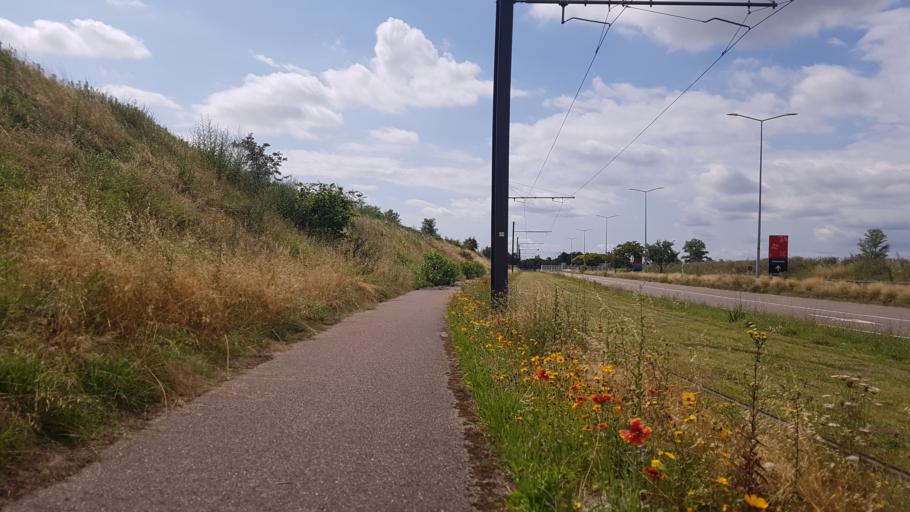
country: FR
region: Rhone-Alpes
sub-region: Departement du Rhone
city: Chassieu
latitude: 45.7374
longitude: 4.9452
